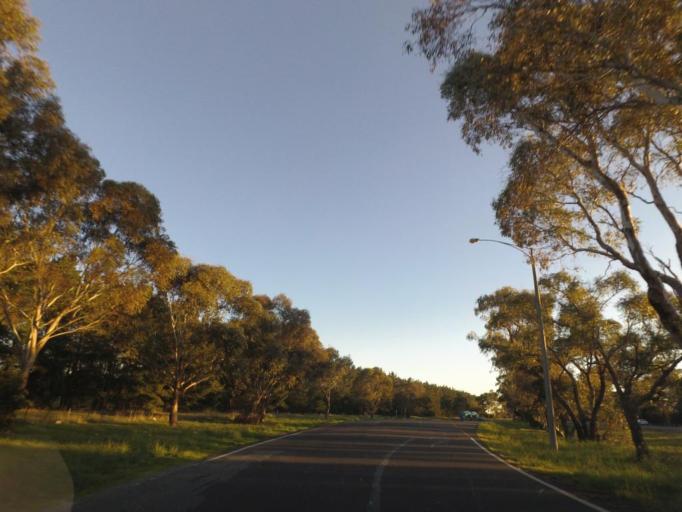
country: AU
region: Victoria
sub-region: Hume
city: Craigieburn
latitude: -37.4966
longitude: 144.9595
